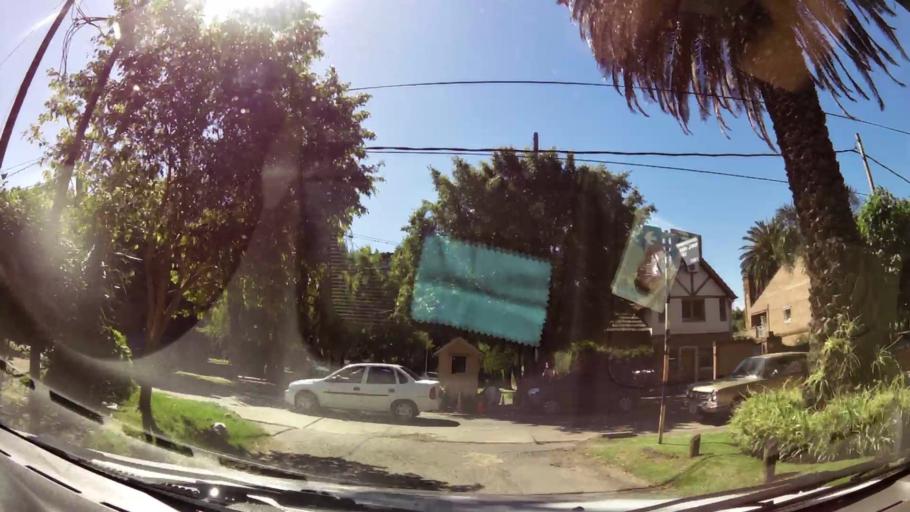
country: AR
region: Buenos Aires
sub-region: Partido de San Isidro
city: San Isidro
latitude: -34.4598
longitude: -58.5210
